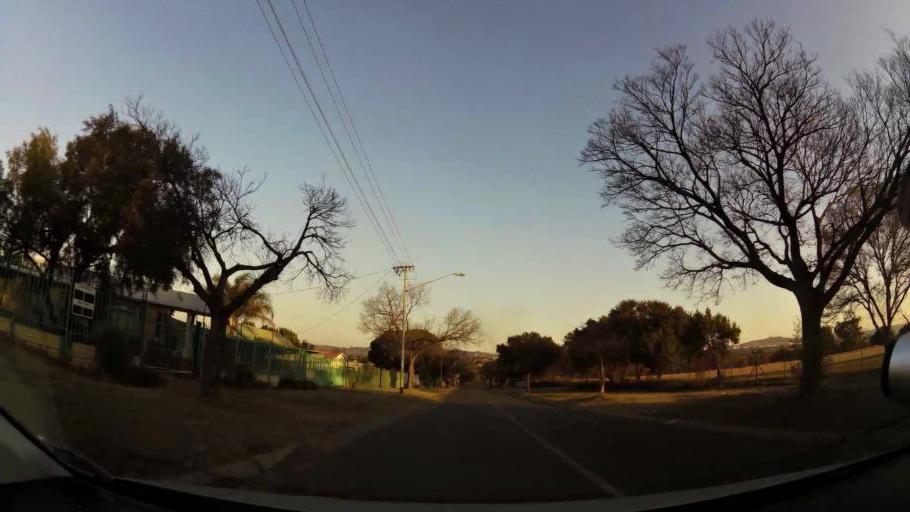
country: ZA
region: Gauteng
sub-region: City of Tshwane Metropolitan Municipality
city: Pretoria
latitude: -25.7442
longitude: 28.1256
